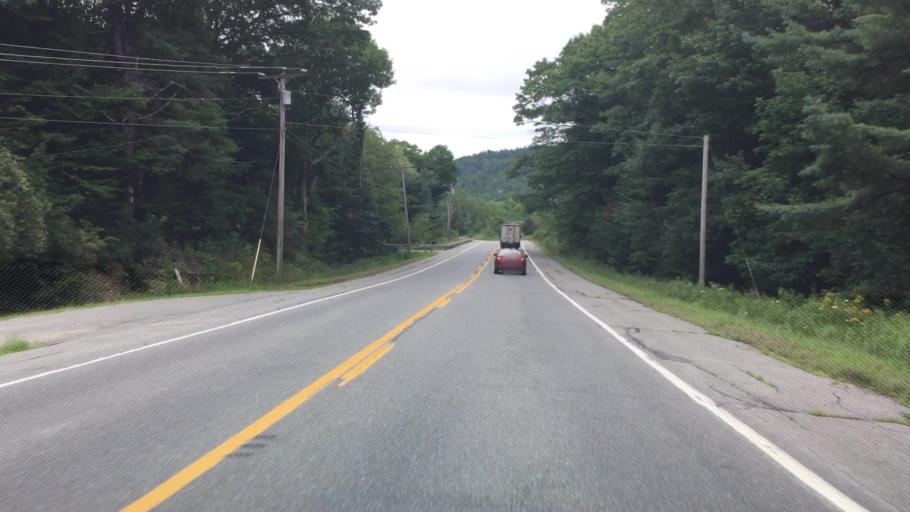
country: US
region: Maine
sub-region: Waldo County
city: Frankfort
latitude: 44.5725
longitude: -68.8630
